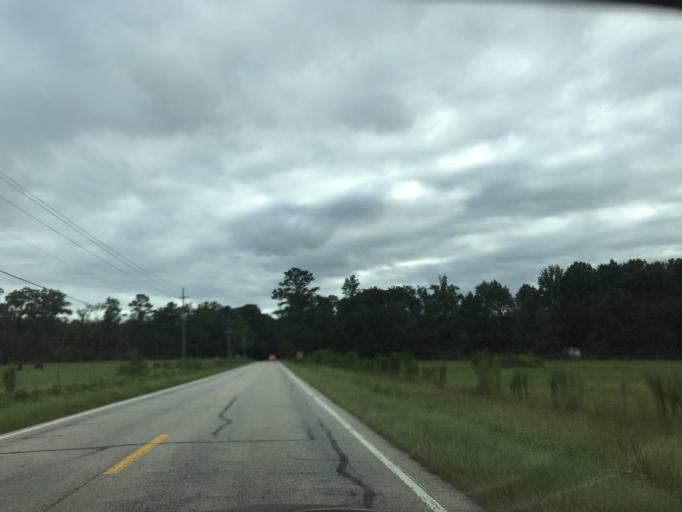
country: US
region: North Carolina
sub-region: Wake County
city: Garner
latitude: 35.5759
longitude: -78.5847
